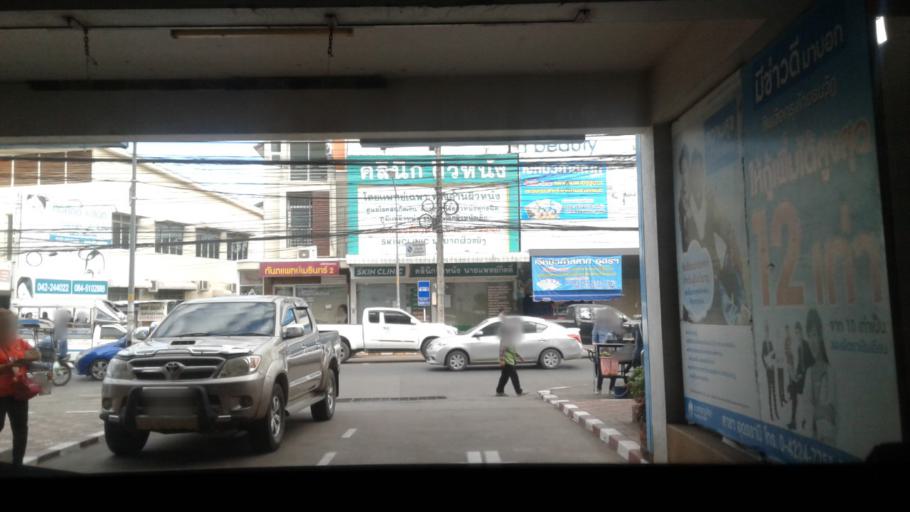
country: TH
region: Changwat Udon Thani
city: Udon Thani
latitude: 17.4187
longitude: 102.7909
